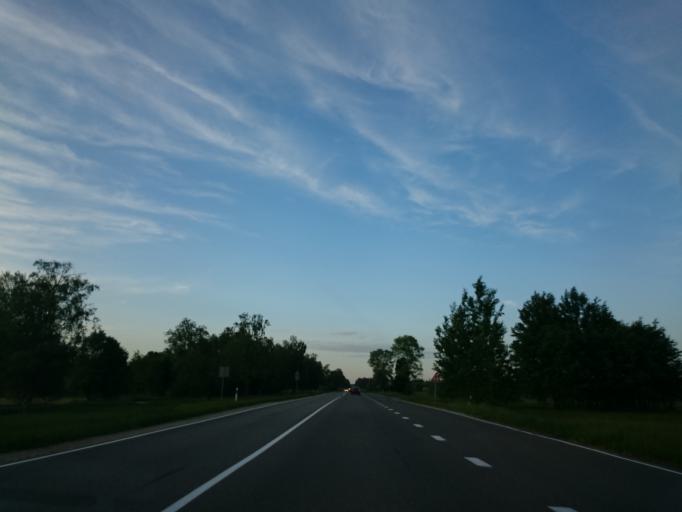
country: LV
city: Tireli
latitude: 56.8429
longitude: 23.5884
